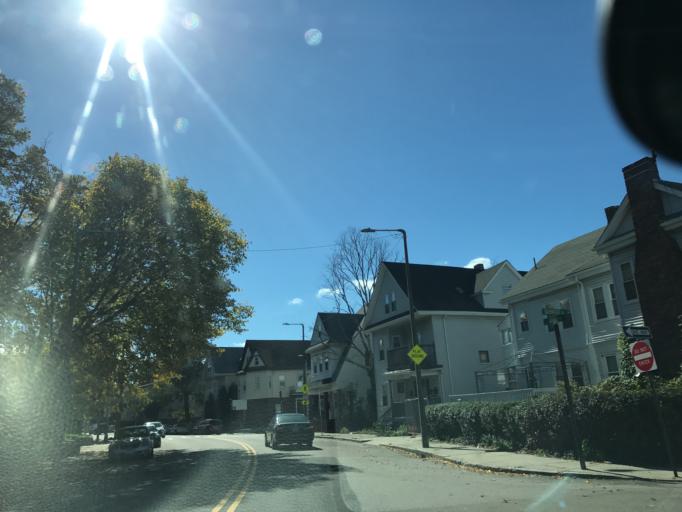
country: US
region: Massachusetts
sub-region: Suffolk County
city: South Boston
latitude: 42.2921
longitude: -71.0574
